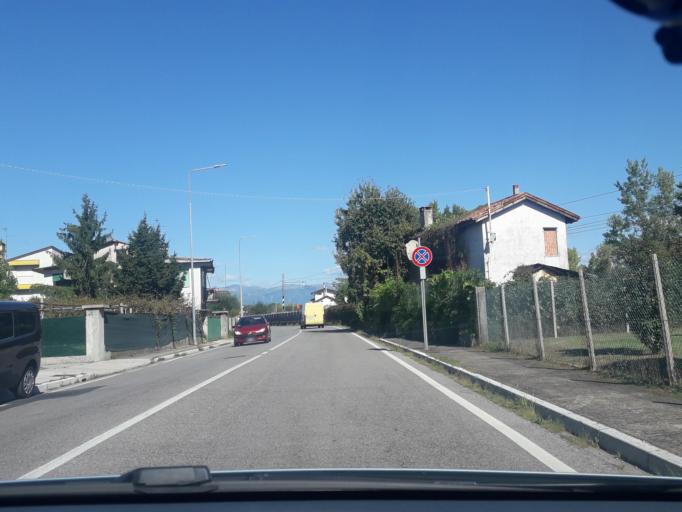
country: IT
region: Friuli Venezia Giulia
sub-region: Provincia di Udine
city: Basaldella
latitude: 46.0384
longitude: 13.2343
